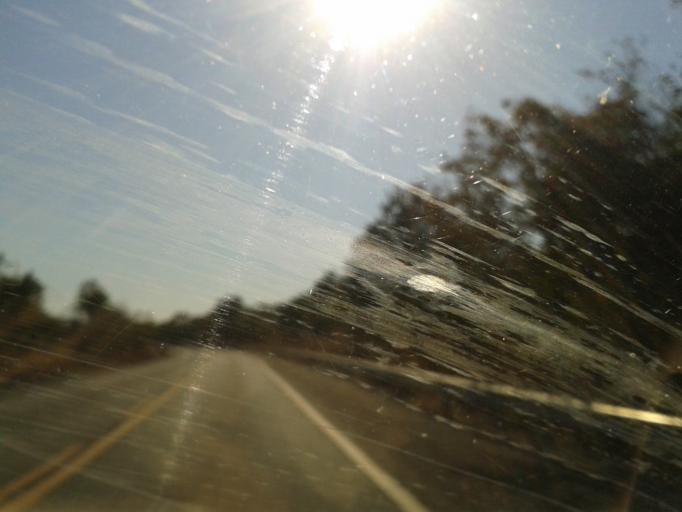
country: BR
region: Goias
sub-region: Mozarlandia
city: Mozarlandia
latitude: -14.9297
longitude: -50.5566
